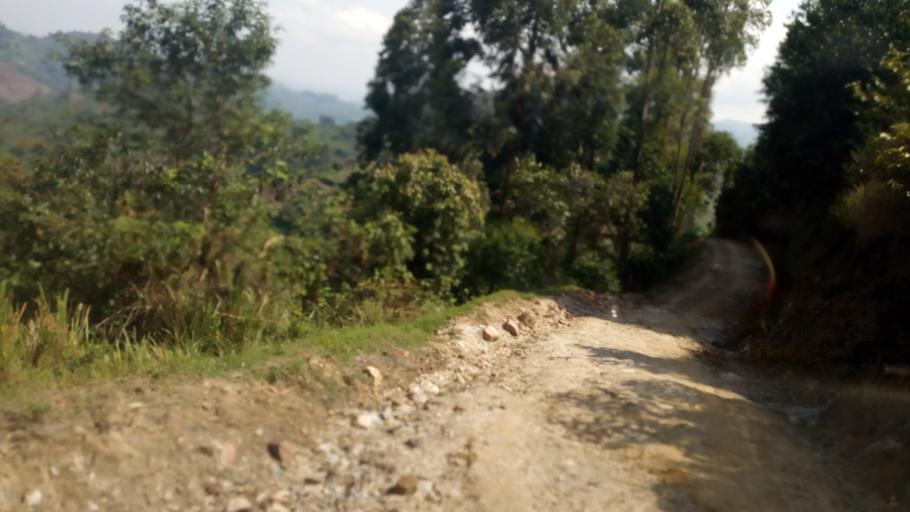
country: UG
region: Western Region
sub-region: Kisoro District
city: Kisoro
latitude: -1.1007
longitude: 29.5873
